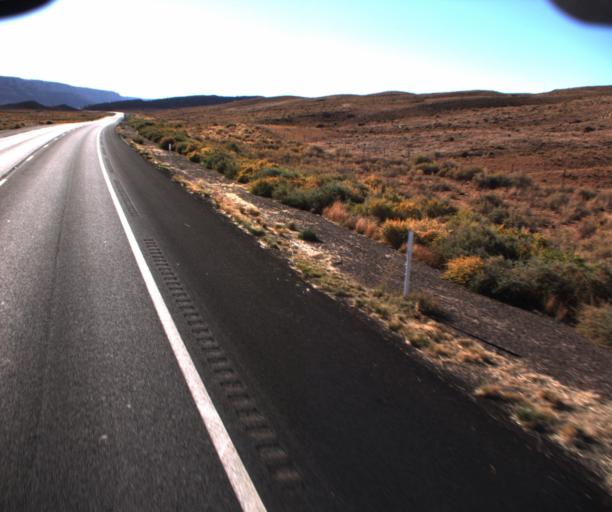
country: US
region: Arizona
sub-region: Coconino County
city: LeChee
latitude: 36.5283
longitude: -111.6044
